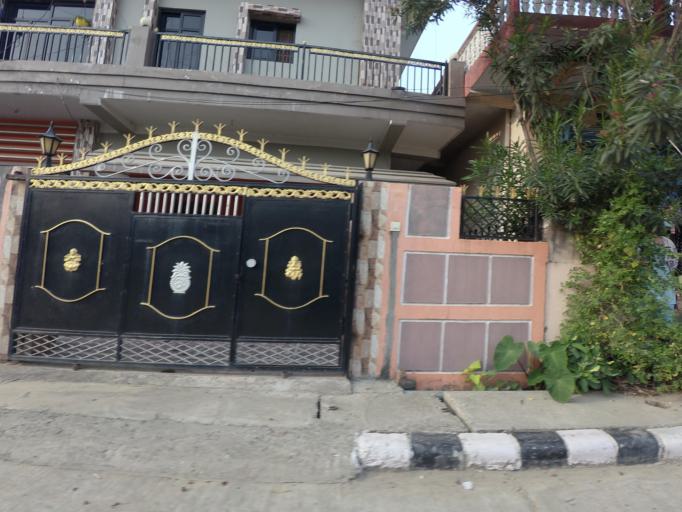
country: NP
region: Western Region
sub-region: Lumbini Zone
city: Bhairahawa
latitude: 27.5110
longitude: 83.4571
